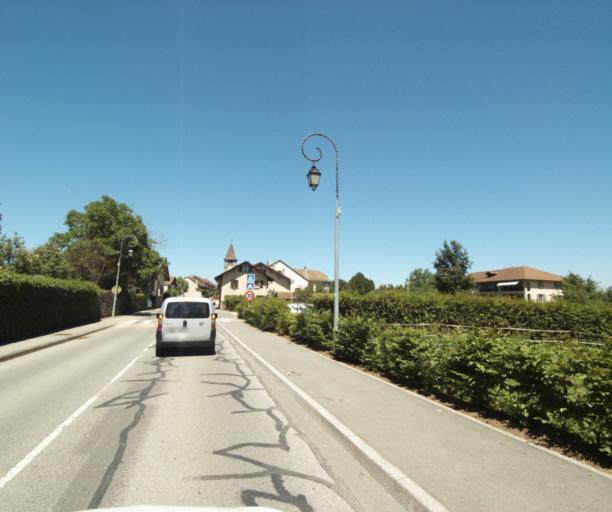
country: FR
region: Rhone-Alpes
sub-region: Departement de la Haute-Savoie
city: Veigy-Foncenex
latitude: 46.2681
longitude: 6.2555
